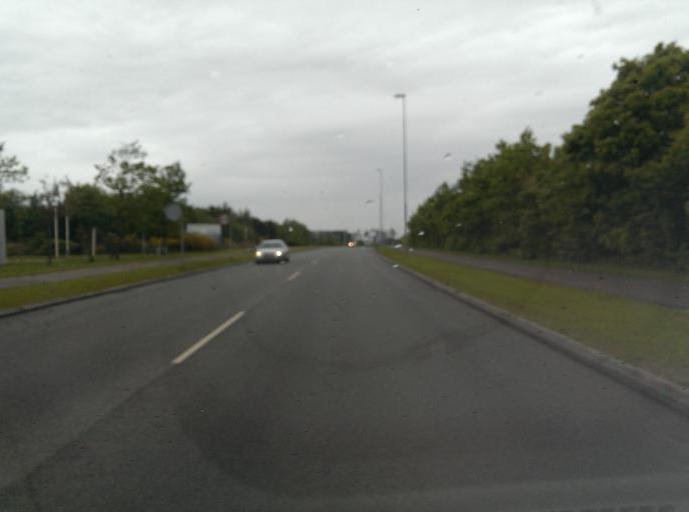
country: DK
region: South Denmark
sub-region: Esbjerg Kommune
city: Esbjerg
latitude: 55.5119
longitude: 8.4670
